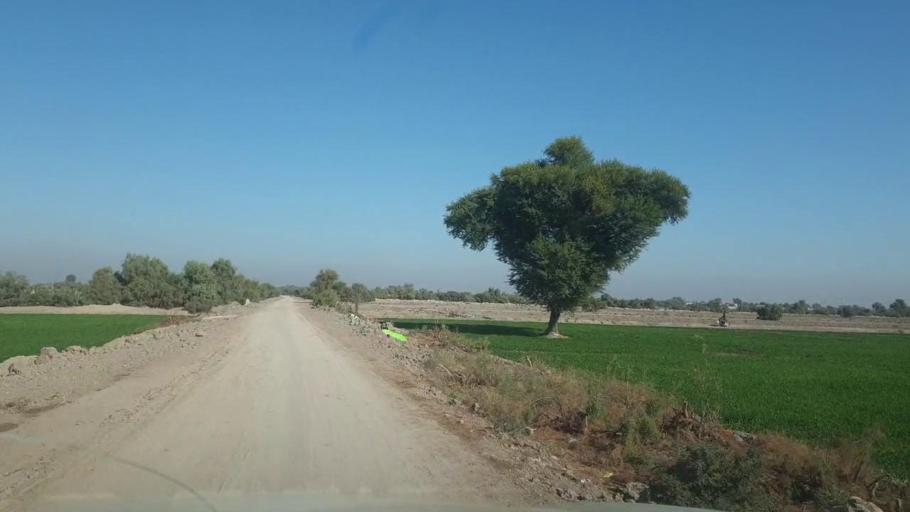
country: PK
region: Sindh
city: Bhan
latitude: 26.5417
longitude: 67.6542
